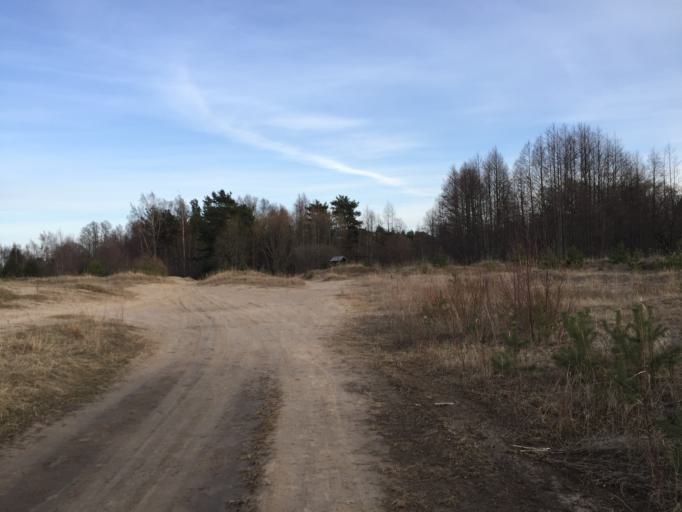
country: LV
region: Salacgrivas
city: Ainazi
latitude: 57.8681
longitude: 24.3541
